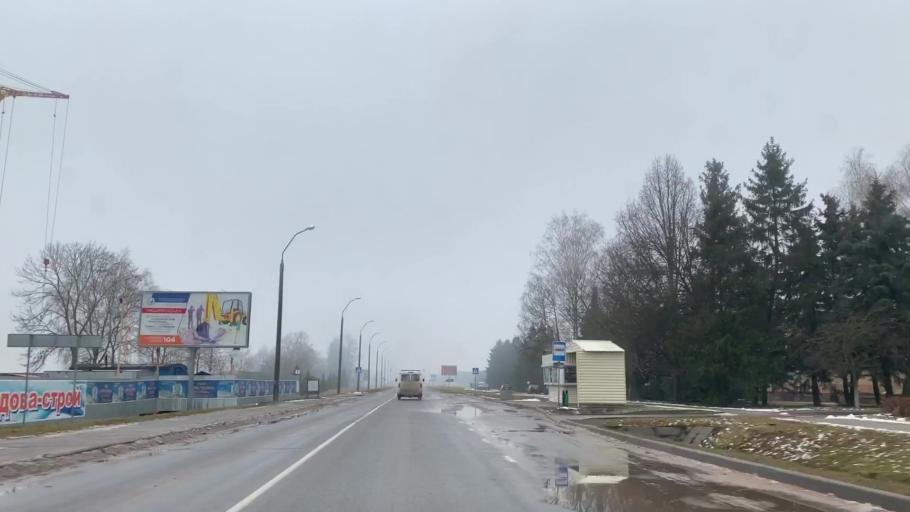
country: BY
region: Minsk
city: Nyasvizh
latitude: 53.2351
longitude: 26.6451
